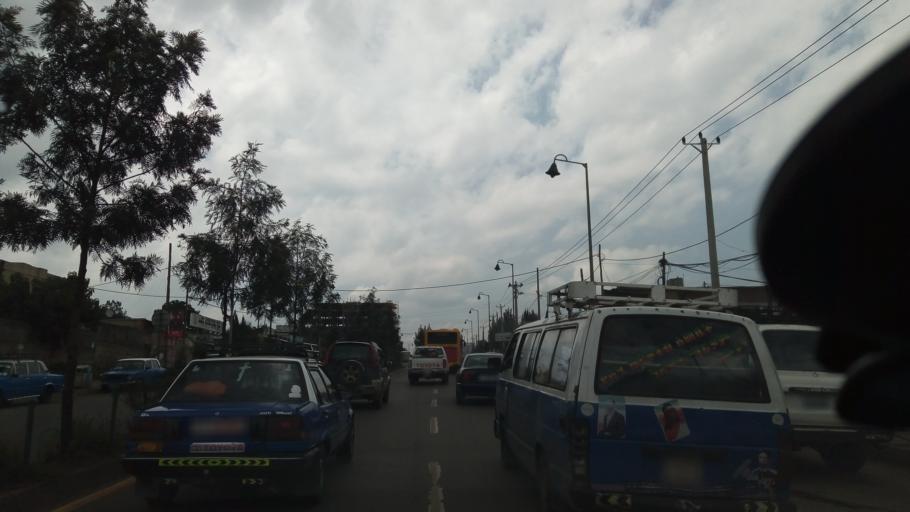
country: ET
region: Adis Abeba
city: Addis Ababa
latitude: 8.9919
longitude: 38.7182
